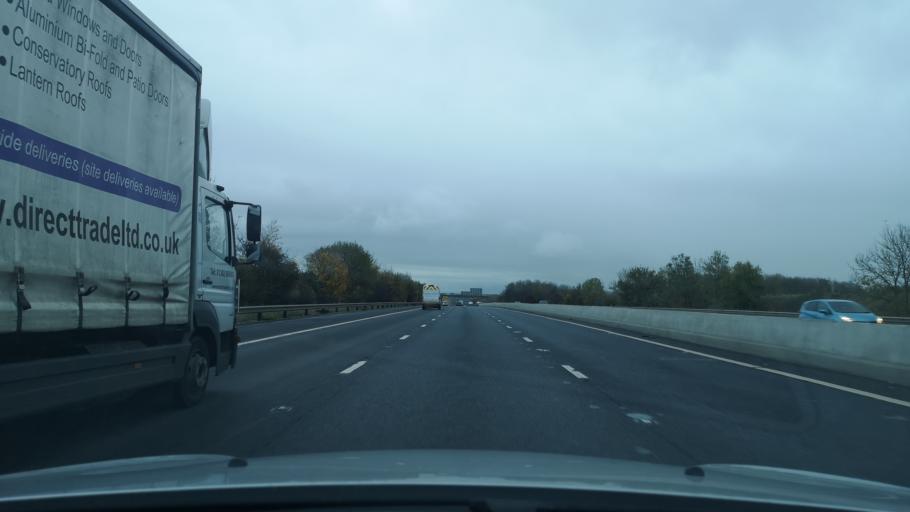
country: GB
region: England
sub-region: City and Borough of Wakefield
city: Knottingley
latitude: 53.6929
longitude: -1.2385
